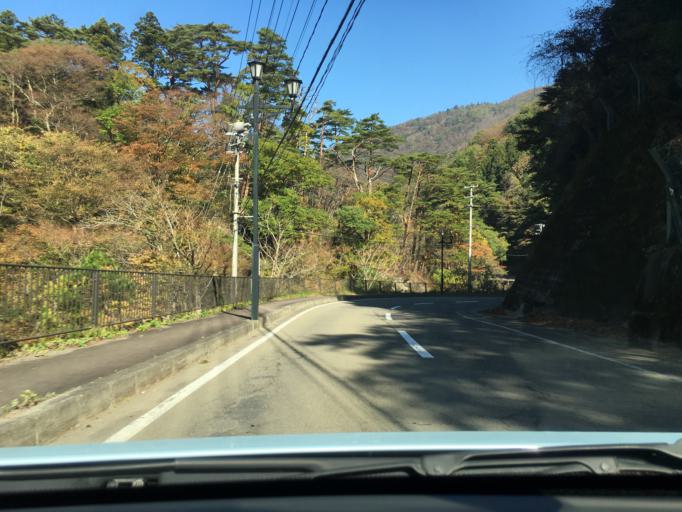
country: JP
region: Fukushima
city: Inawashiro
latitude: 37.4715
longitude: 139.9626
